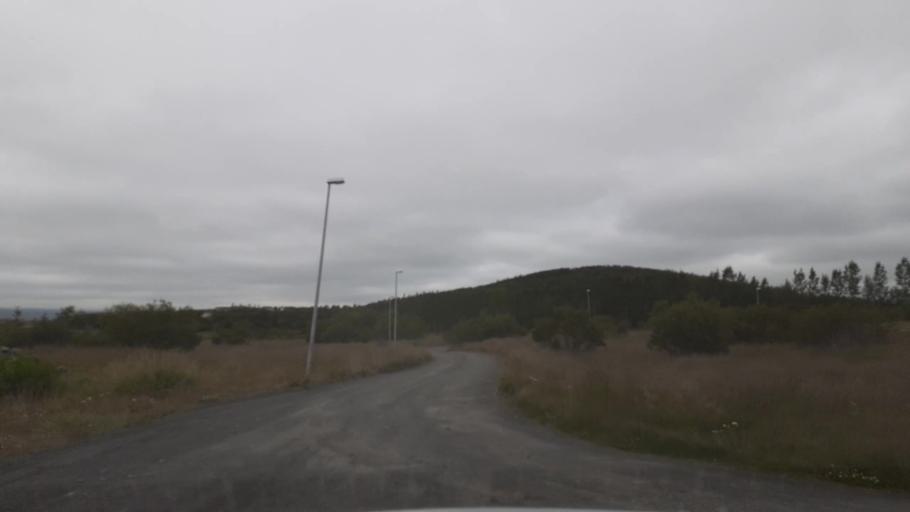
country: IS
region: Northwest
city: Saudarkrokur
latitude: 65.5494
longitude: -19.4554
